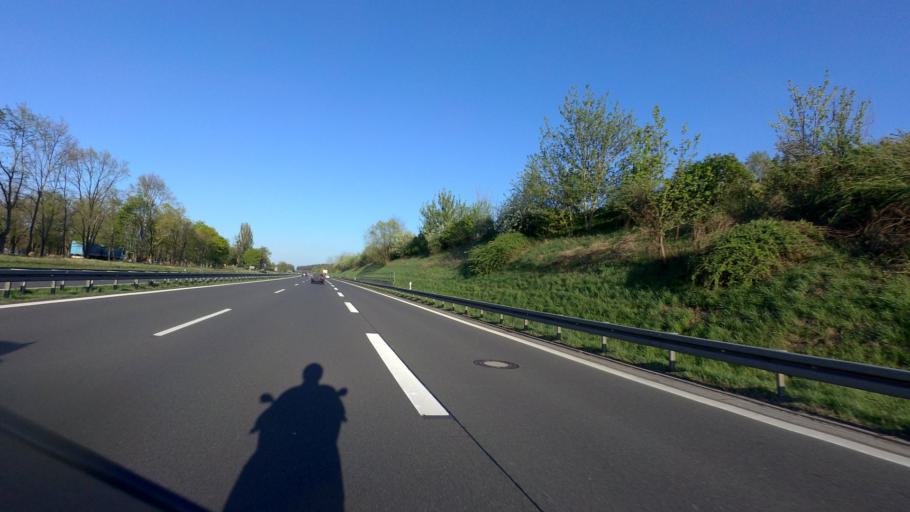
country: DE
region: Brandenburg
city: Dallgow-Doeberitz
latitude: 52.5339
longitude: 13.0504
